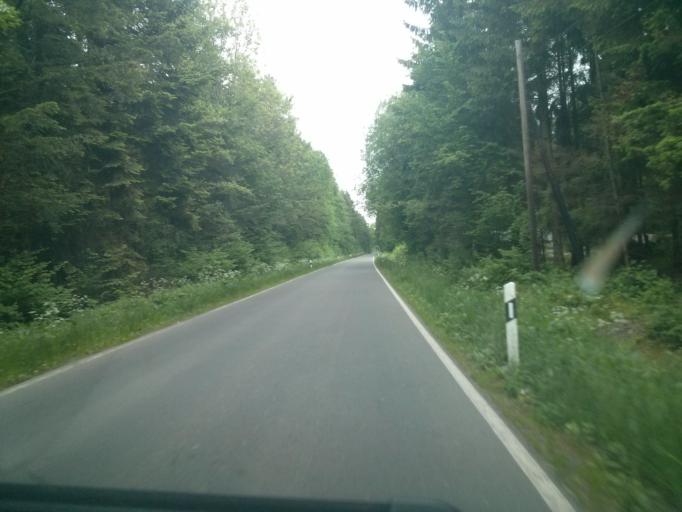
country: DE
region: Mecklenburg-Vorpommern
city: Velgast
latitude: 54.2541
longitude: 12.8224
